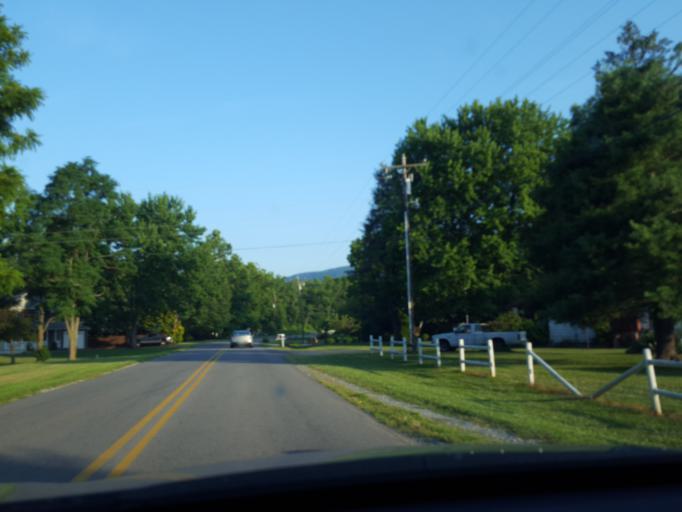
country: US
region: Virginia
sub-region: Augusta County
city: Lyndhurst
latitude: 37.9848
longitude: -78.9549
